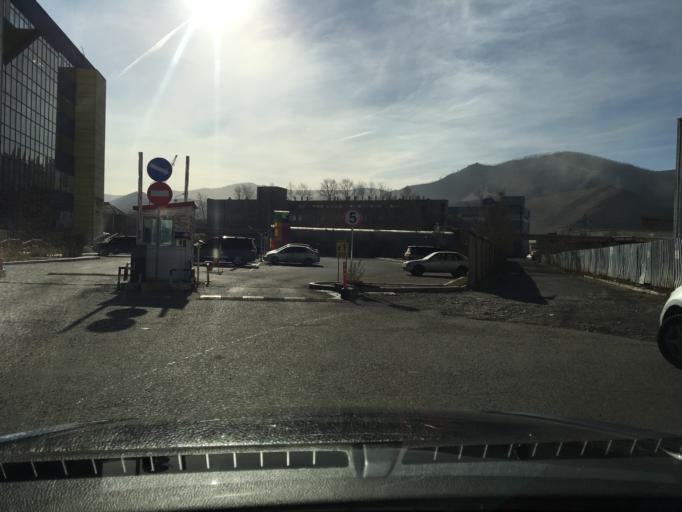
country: MN
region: Ulaanbaatar
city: Ulaanbaatar
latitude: 47.8968
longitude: 106.8882
